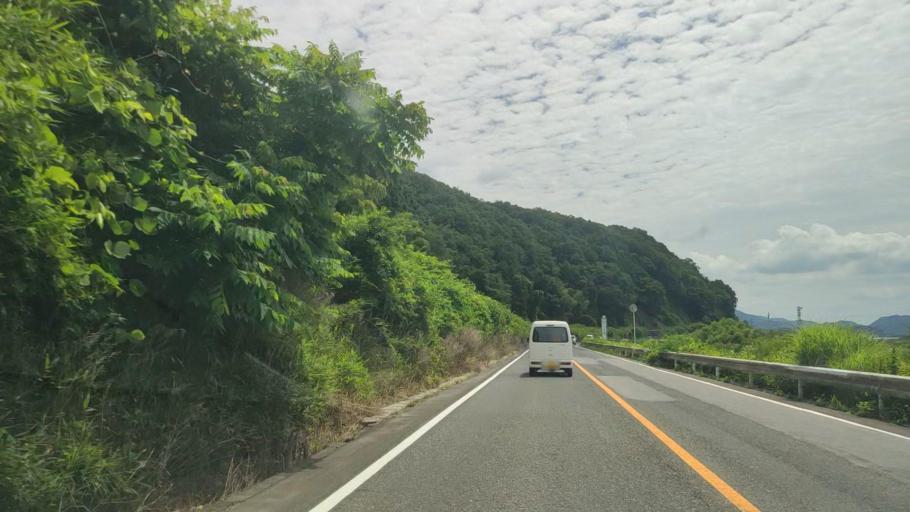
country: JP
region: Okayama
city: Niimi
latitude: 35.0835
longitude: 133.7175
